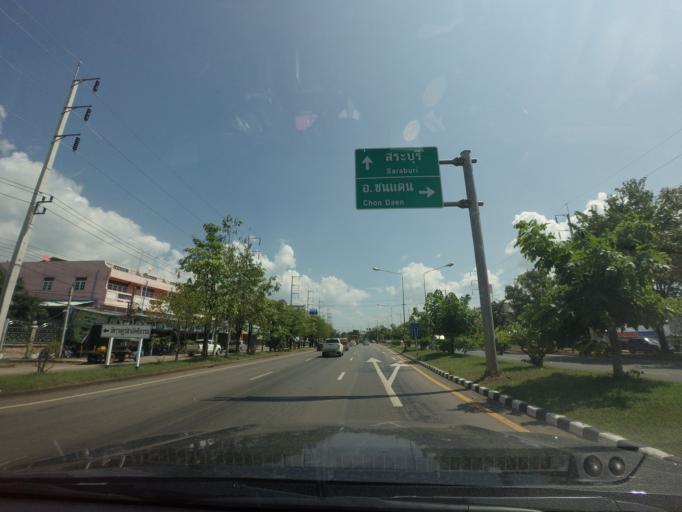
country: TH
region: Phetchabun
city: Nong Phai
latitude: 16.0822
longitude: 101.0573
